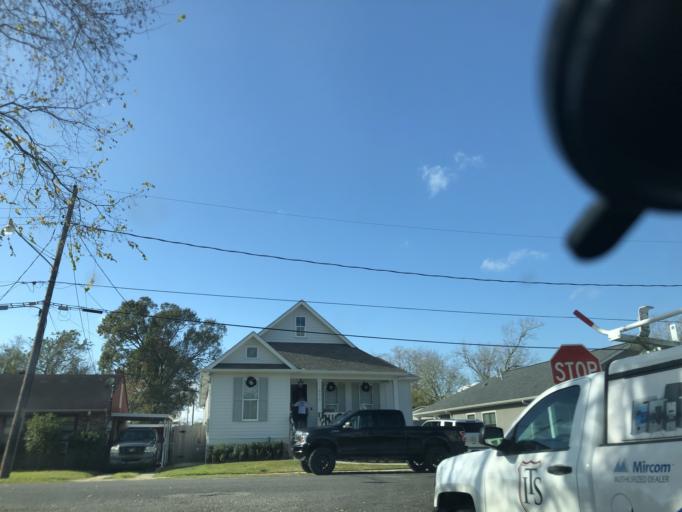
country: US
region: Louisiana
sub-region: Jefferson Parish
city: Metairie Terrace
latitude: 29.9807
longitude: -90.1629
